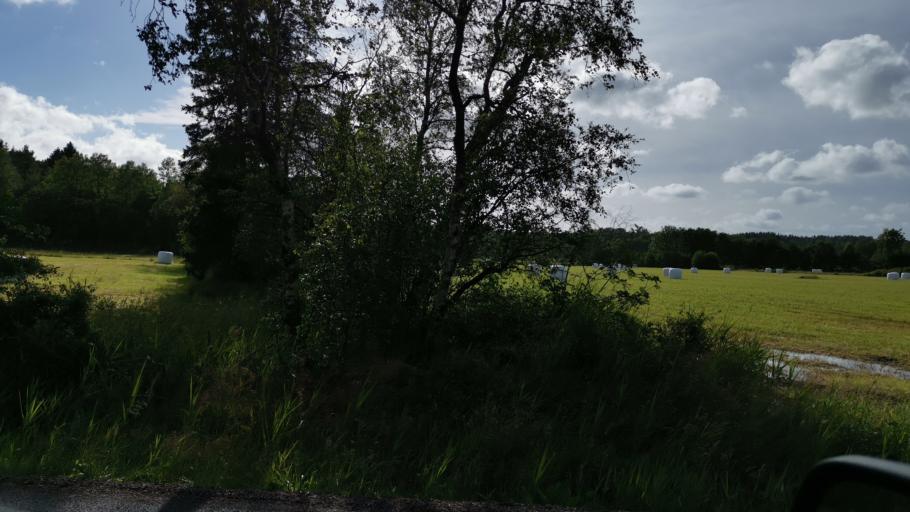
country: SE
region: Vaestra Goetaland
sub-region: Orust
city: Henan
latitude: 58.1805
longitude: 11.6063
